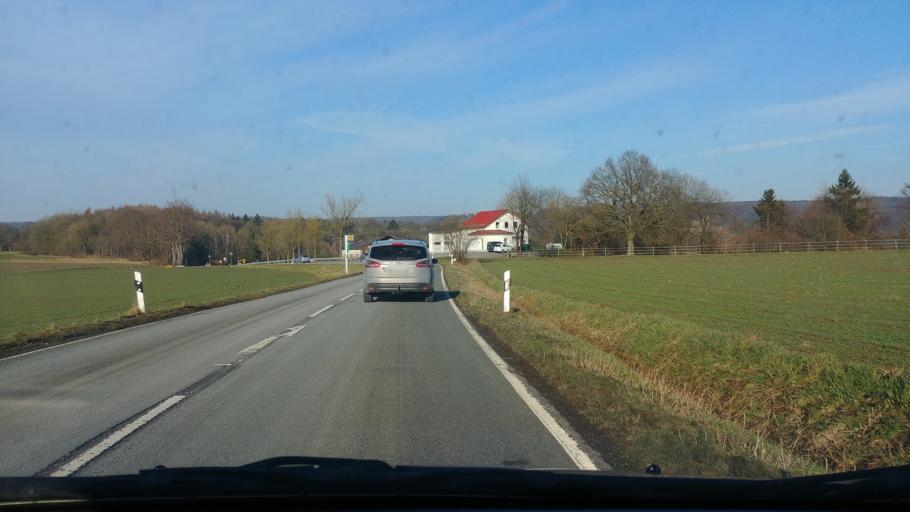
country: DE
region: Lower Saxony
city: Bad Karlshafen
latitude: 51.6248
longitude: 9.4466
